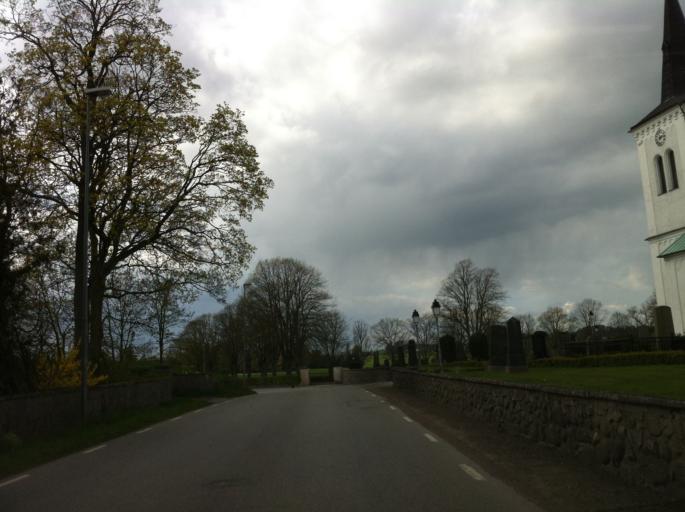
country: SE
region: Skane
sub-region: Kavlinge Kommun
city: Kaevlinge
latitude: 55.8220
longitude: 13.1050
